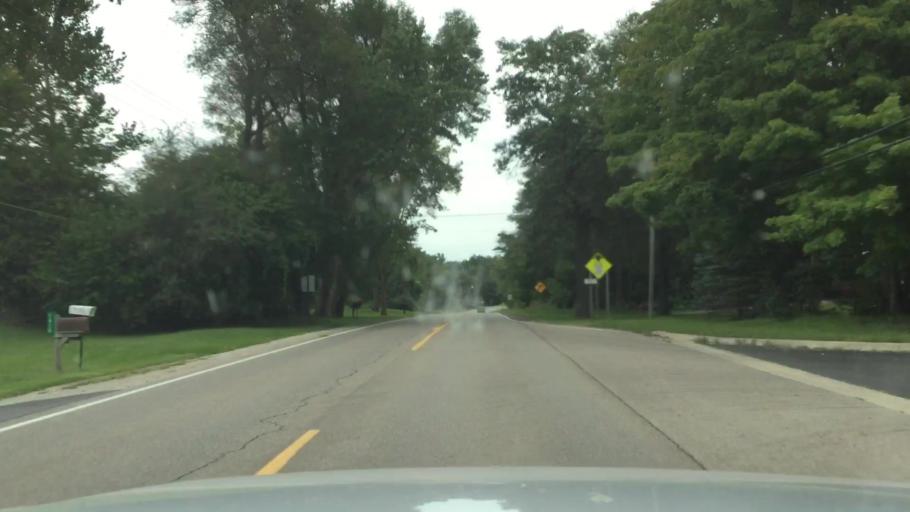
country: US
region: Michigan
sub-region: Genesee County
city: Argentine
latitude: 42.8066
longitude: -83.8188
